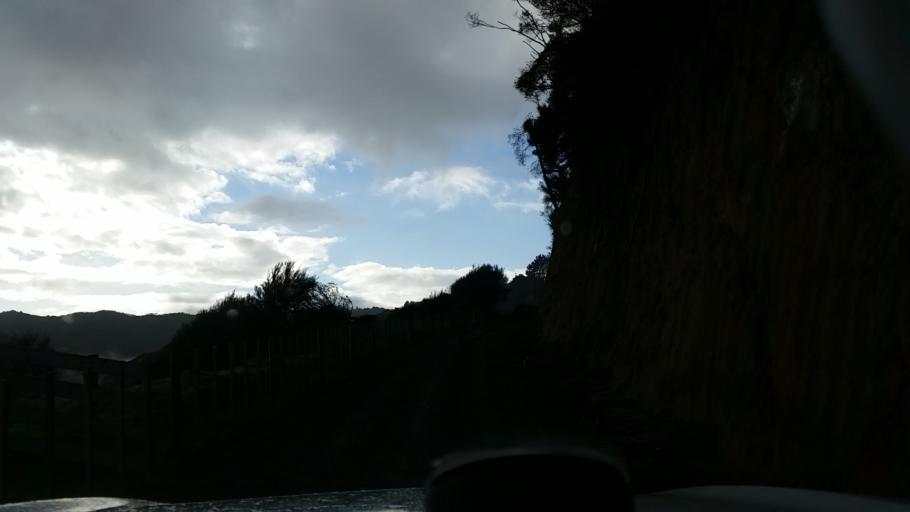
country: NZ
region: Taranaki
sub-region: South Taranaki District
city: Eltham
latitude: -39.4083
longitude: 174.5386
